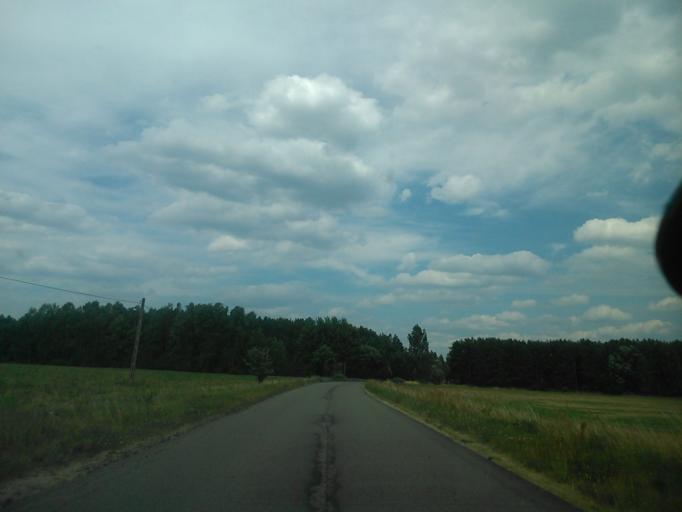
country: PL
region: Masovian Voivodeship
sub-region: Powiat ostrolecki
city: Czarnia
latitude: 53.3743
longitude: 21.1997
